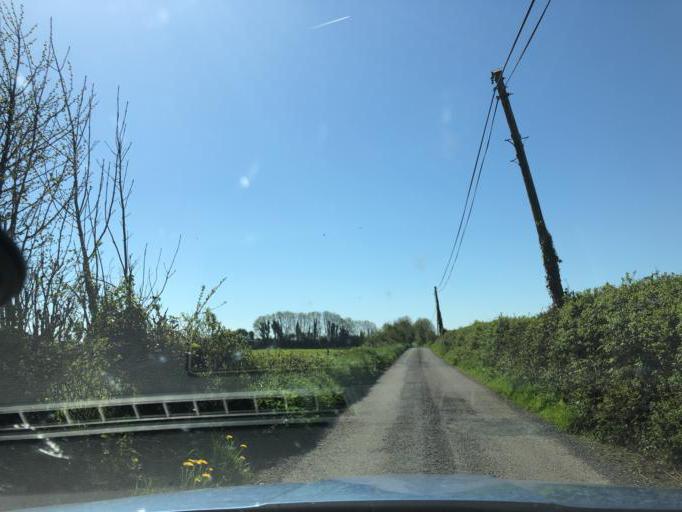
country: IE
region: Connaught
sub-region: County Galway
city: Portumna
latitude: 53.1447
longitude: -8.3387
